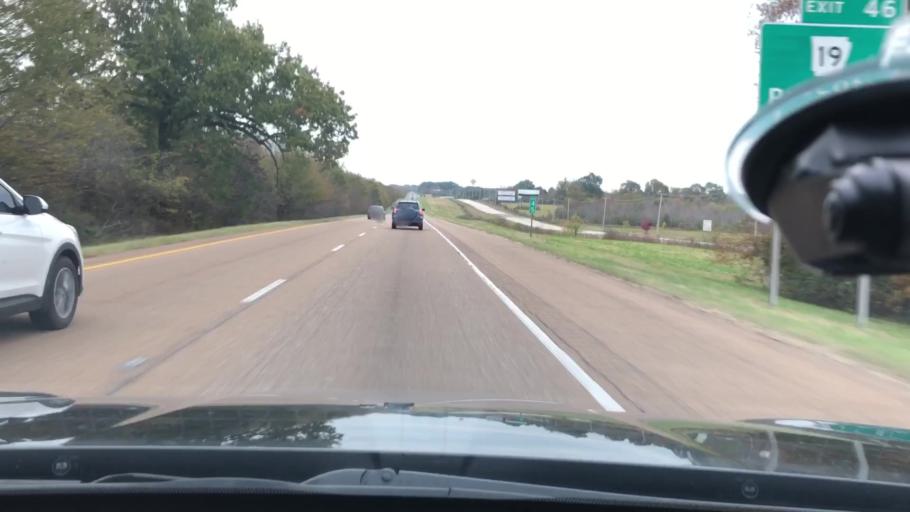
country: US
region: Arkansas
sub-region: Nevada County
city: Prescott
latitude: 33.8193
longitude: -93.4112
